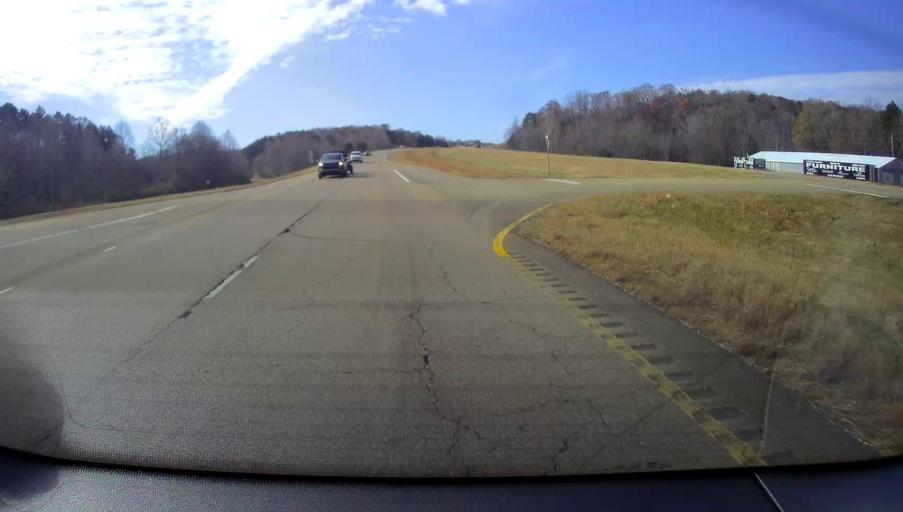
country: US
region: Mississippi
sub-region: Alcorn County
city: Corinth
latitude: 34.9325
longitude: -88.7543
